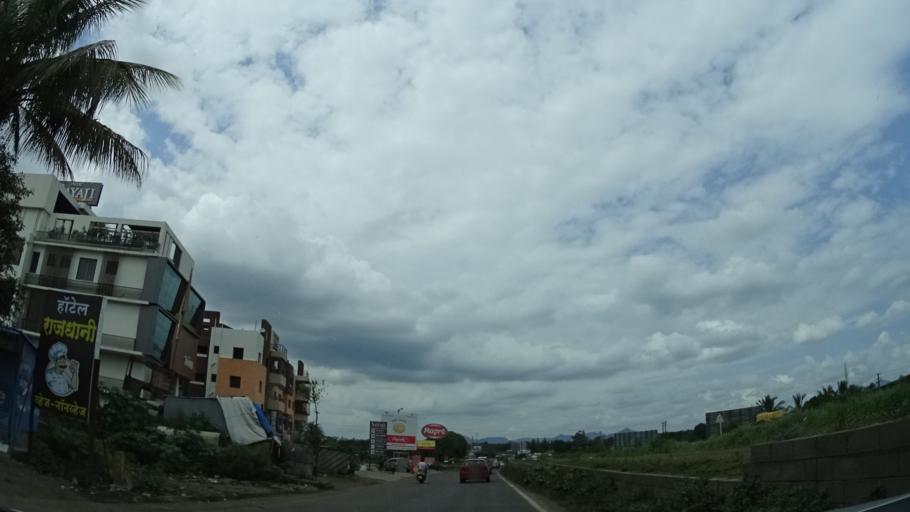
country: IN
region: Maharashtra
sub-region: Satara Division
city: Satara
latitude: 17.7088
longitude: 74.0264
